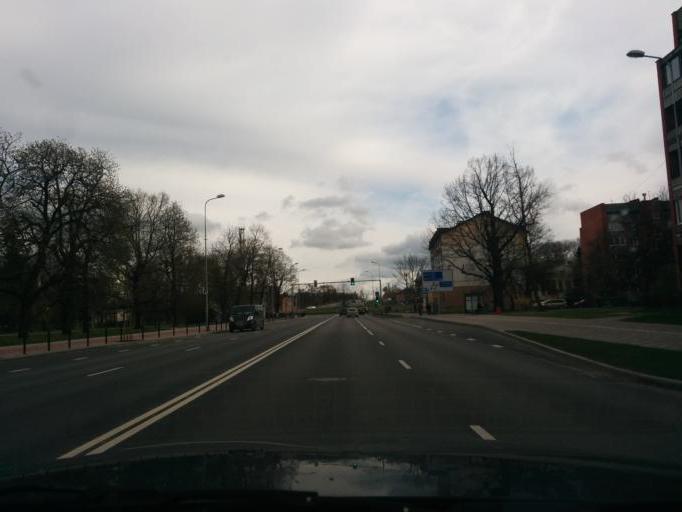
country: LV
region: Jelgava
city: Jelgava
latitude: 56.6429
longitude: 23.7284
